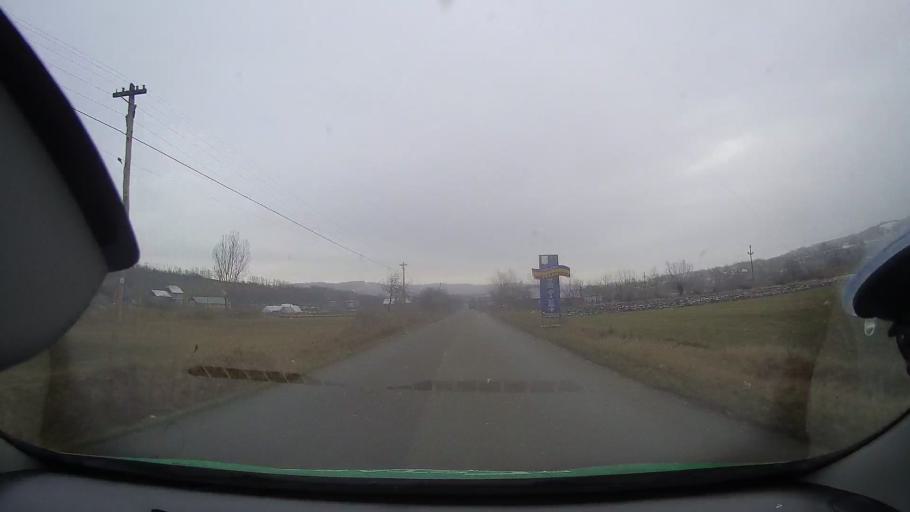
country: RO
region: Alba
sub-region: Comuna Farau
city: Farau
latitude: 46.3393
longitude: 23.9916
